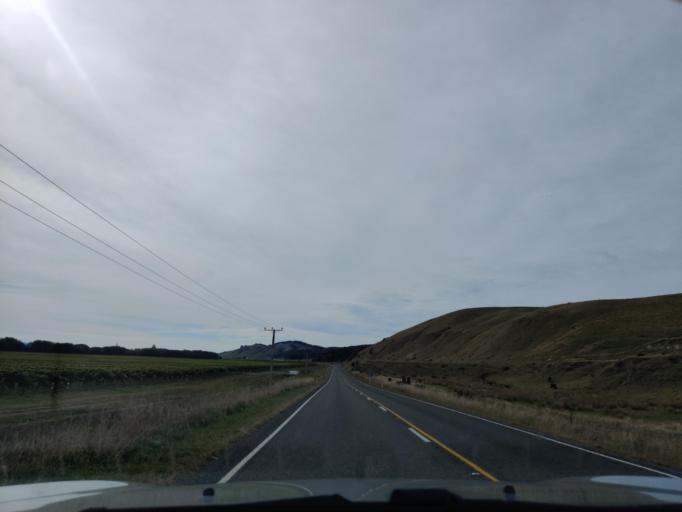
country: NZ
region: Marlborough
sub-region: Marlborough District
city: Blenheim
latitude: -41.5341
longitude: 173.6477
